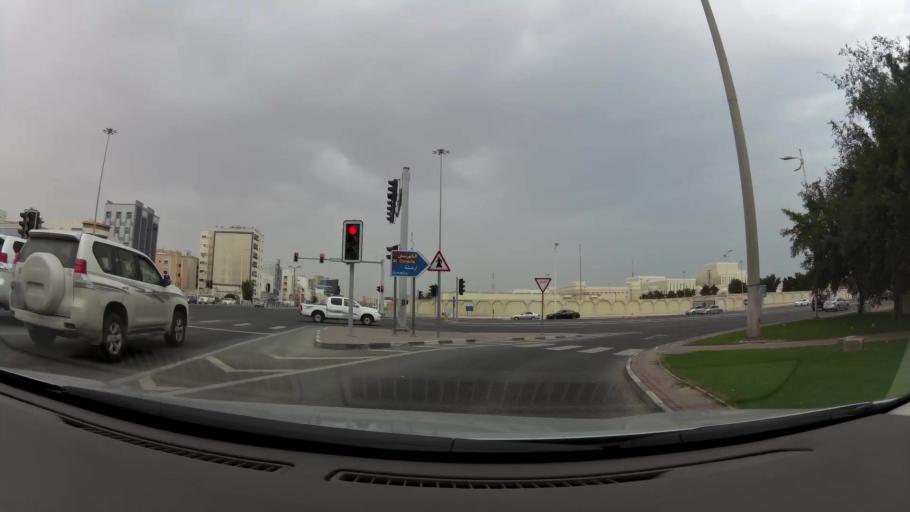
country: QA
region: Baladiyat ad Dawhah
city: Doha
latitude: 25.3001
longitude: 51.5031
